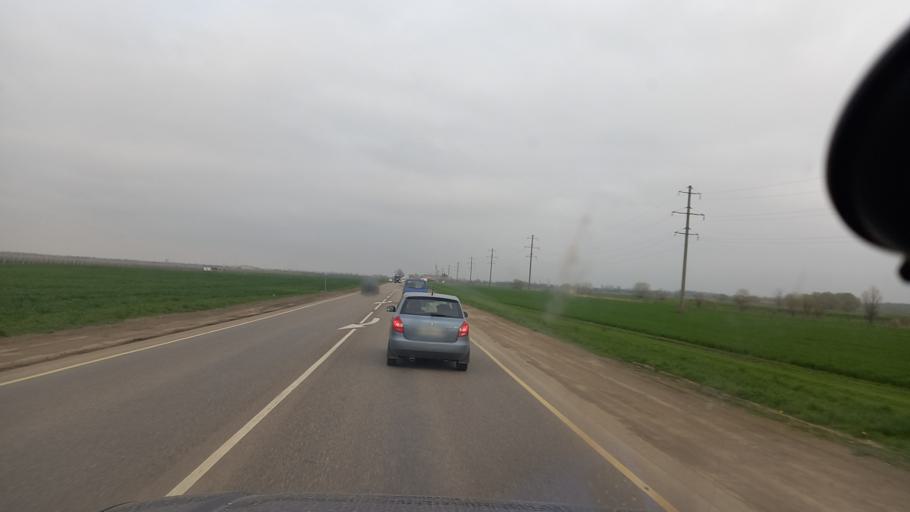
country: RU
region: Krasnodarskiy
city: Slavyansk-na-Kubani
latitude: 45.2411
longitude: 38.0239
